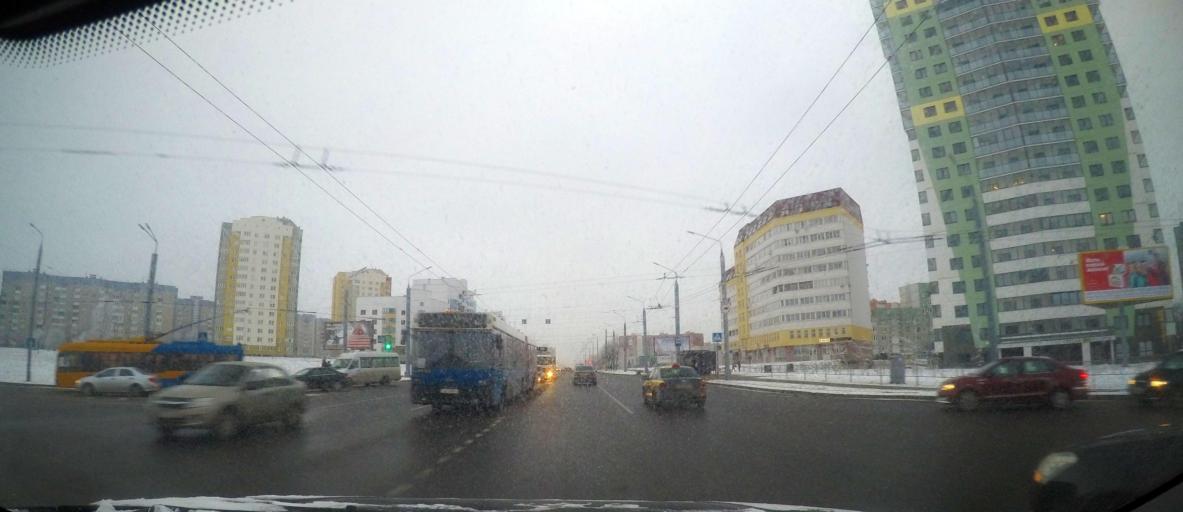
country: BY
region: Grodnenskaya
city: Hrodna
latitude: 53.6526
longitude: 23.8533
